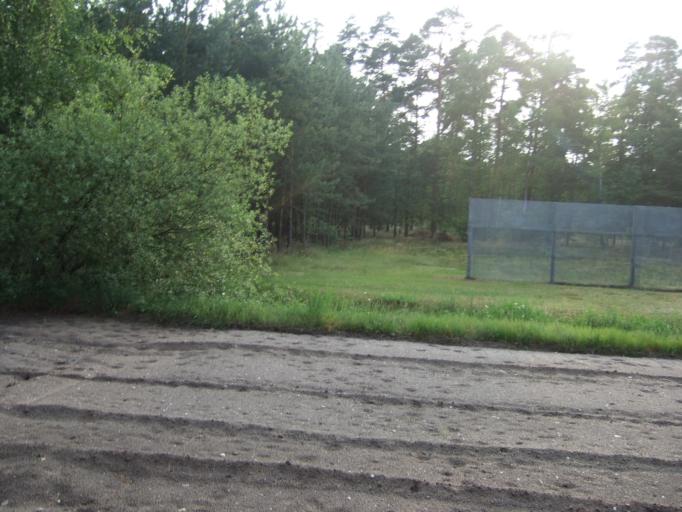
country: DE
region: Lower Saxony
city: Brome
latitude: 52.5566
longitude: 10.9432
